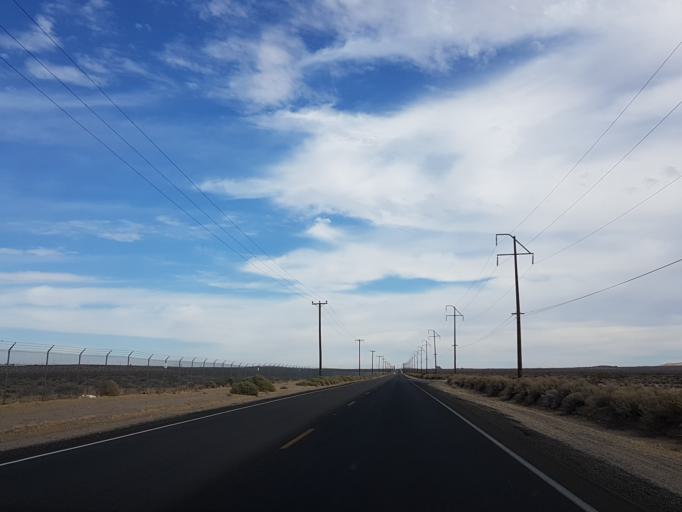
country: US
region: California
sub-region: Kern County
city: Ridgecrest
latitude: 35.6226
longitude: -117.6272
